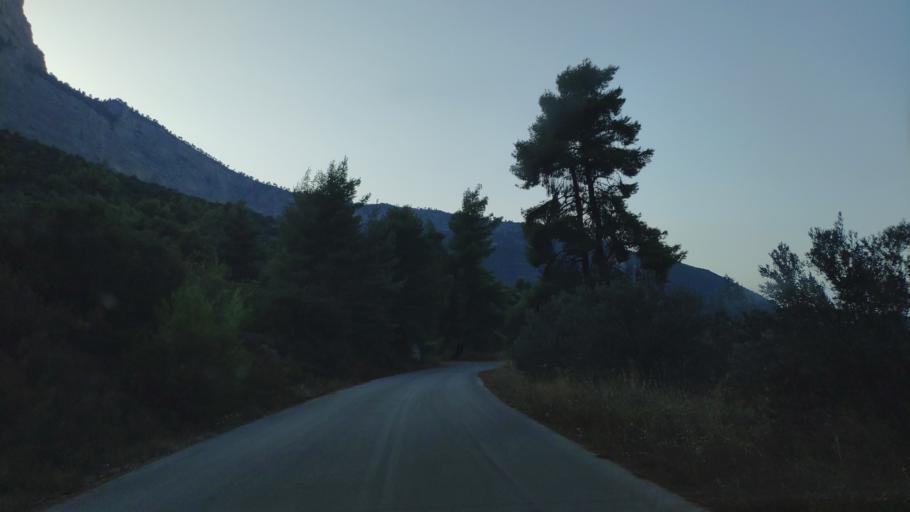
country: GR
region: West Greece
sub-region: Nomos Achaias
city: Aiyira
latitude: 38.0995
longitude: 22.3986
